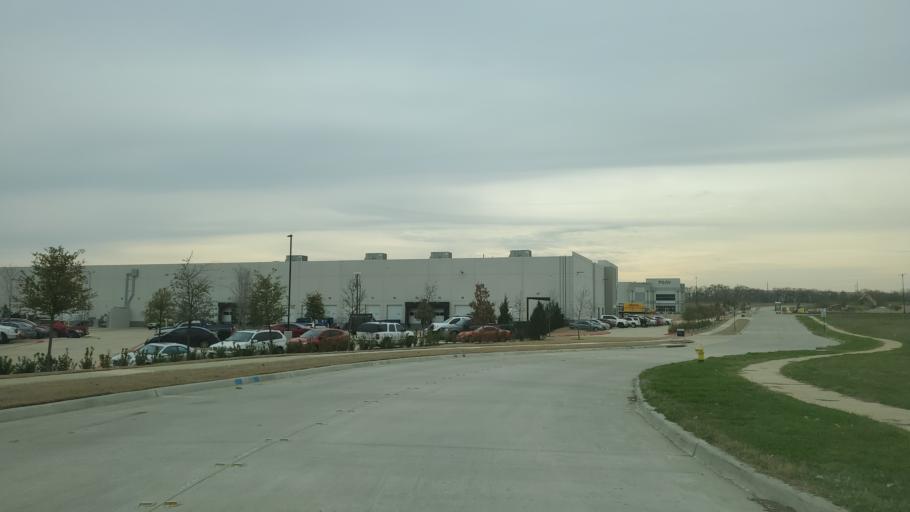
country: US
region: Texas
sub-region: Dallas County
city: Coppell
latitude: 32.9806
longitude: -97.0169
